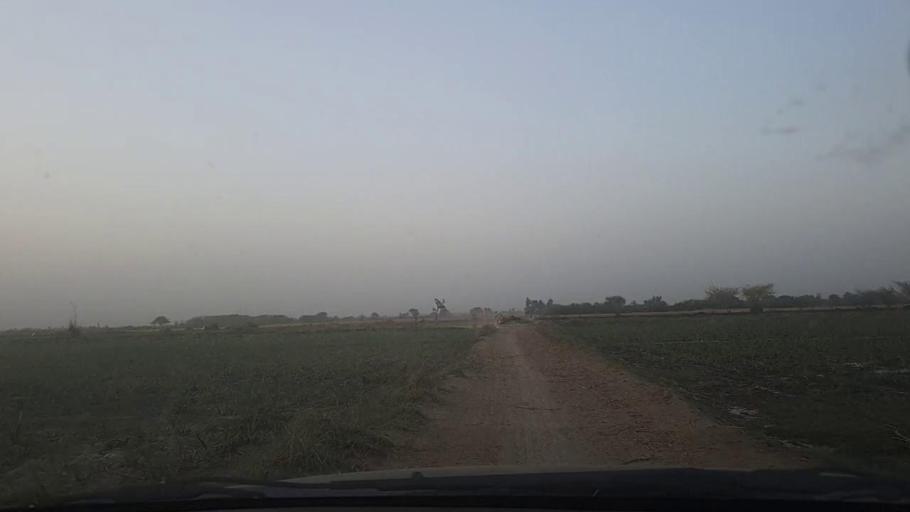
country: PK
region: Sindh
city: Mirpur Sakro
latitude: 24.3833
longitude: 67.6502
